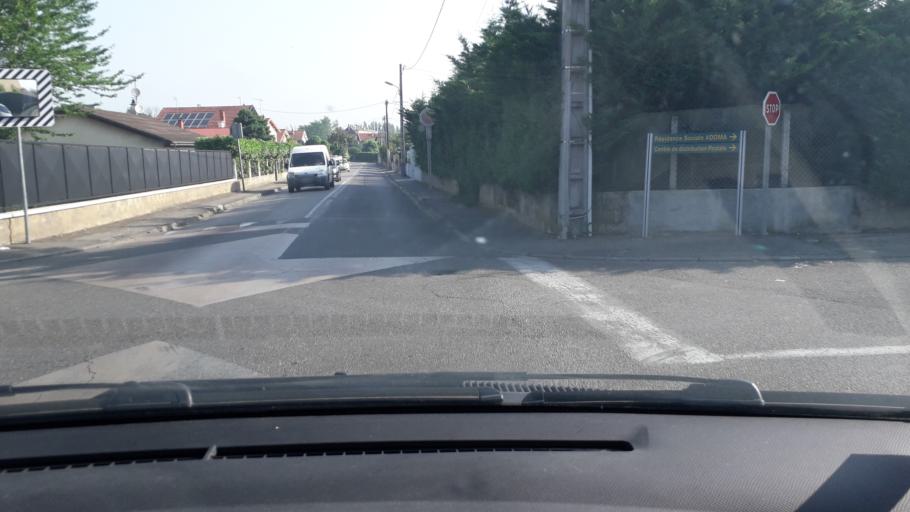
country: FR
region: Rhone-Alpes
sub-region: Departement de l'Isere
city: Pont-de-Cheruy
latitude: 45.7572
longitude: 5.1784
